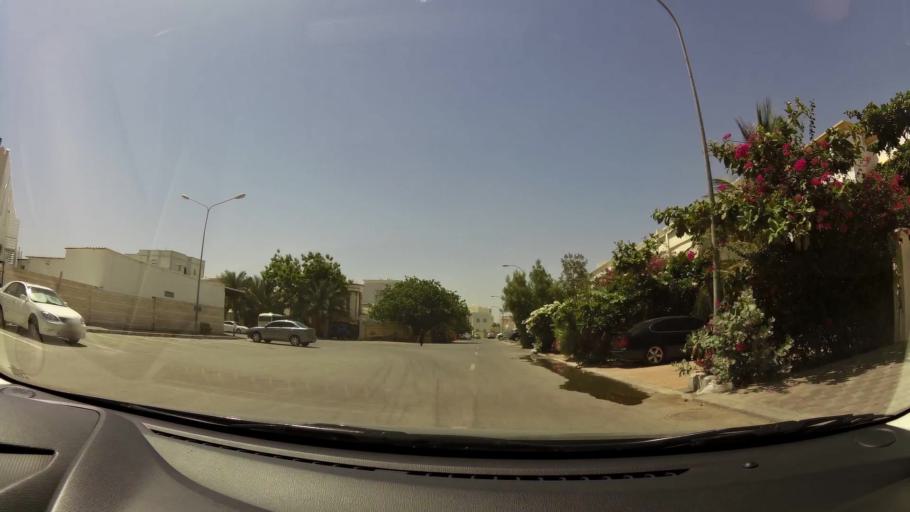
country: OM
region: Muhafazat Masqat
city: As Sib al Jadidah
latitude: 23.6241
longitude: 58.2560
